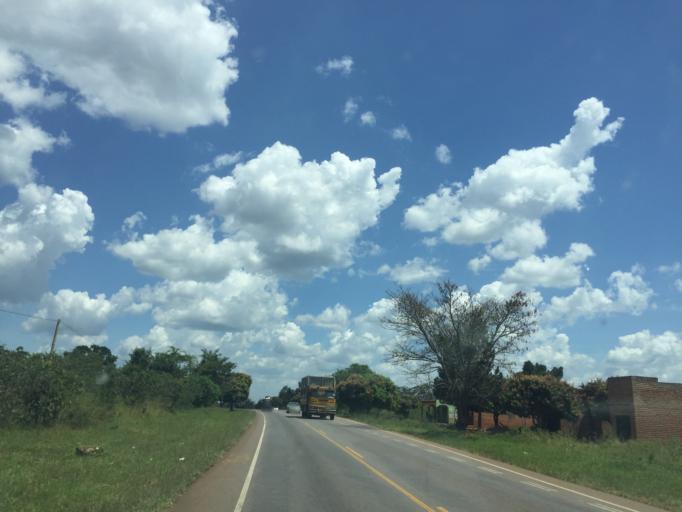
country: UG
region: Central Region
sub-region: Nakasongola District
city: Nakasongola
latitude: 1.3421
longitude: 32.3953
